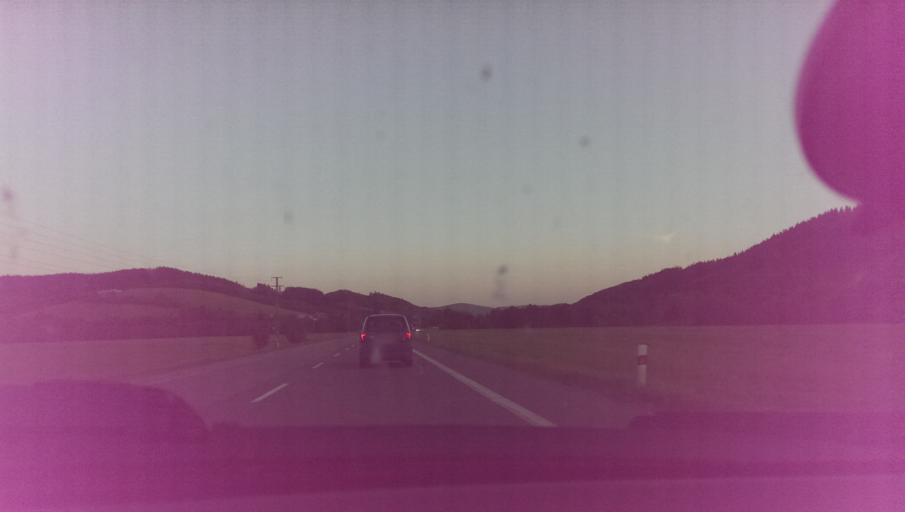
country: CZ
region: Zlin
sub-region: Okres Vsetin
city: Vsetin
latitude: 49.3171
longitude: 18.0046
